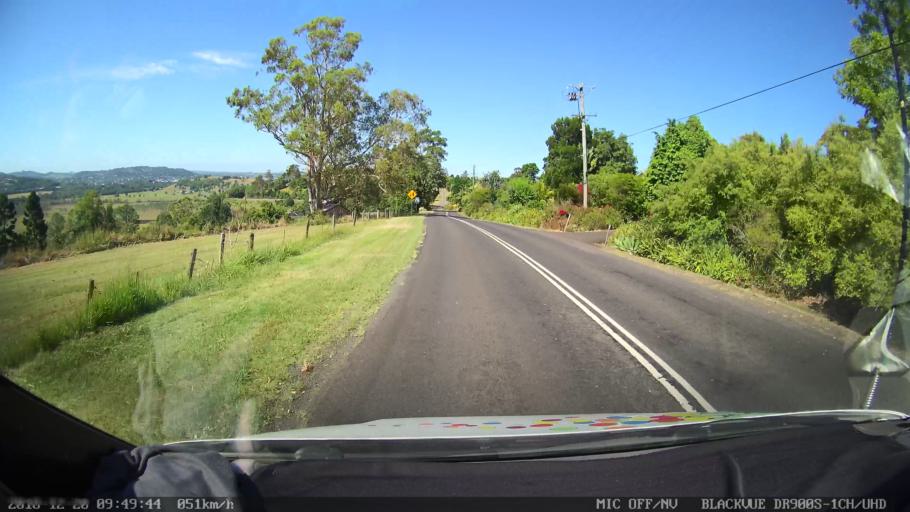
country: AU
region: New South Wales
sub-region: Lismore Municipality
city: Lismore
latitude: -28.7749
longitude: 153.2832
